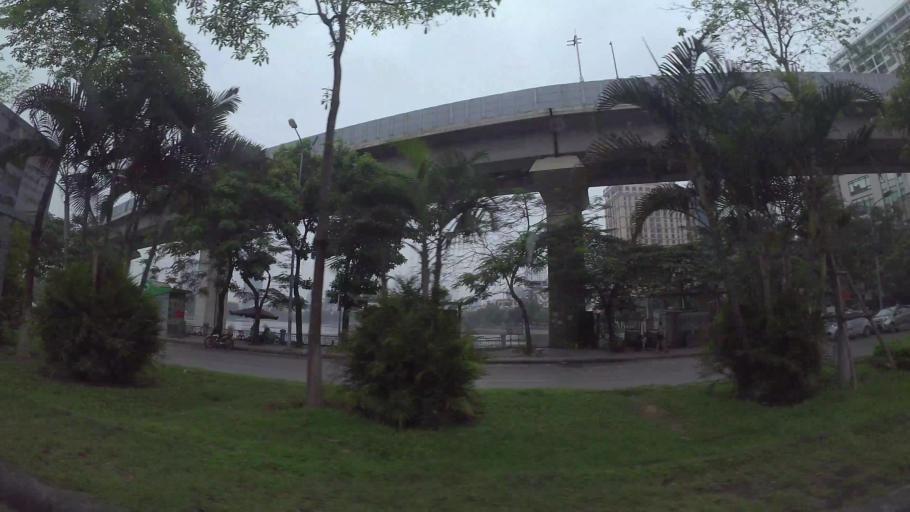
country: VN
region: Ha Noi
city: Dong Da
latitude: 21.0176
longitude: 105.8241
